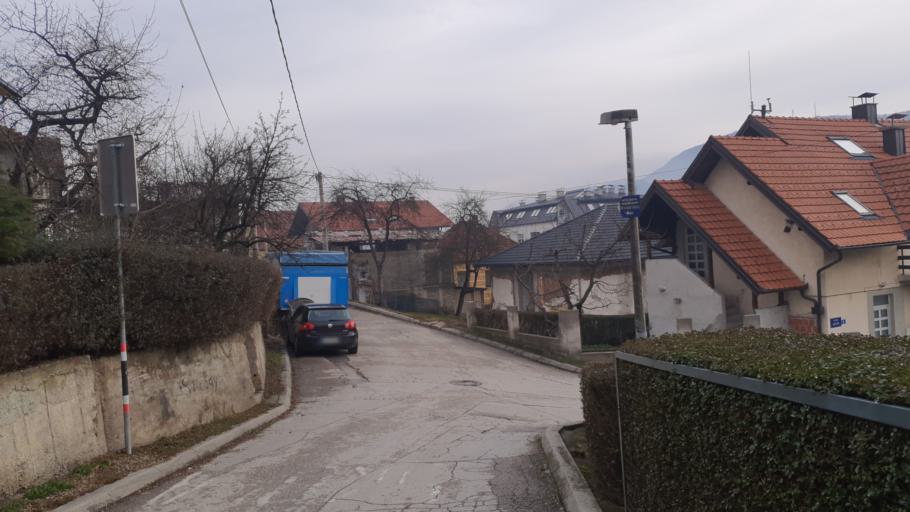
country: RS
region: Central Serbia
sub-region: Zlatiborski Okrug
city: Uzice
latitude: 43.8614
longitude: 19.8185
